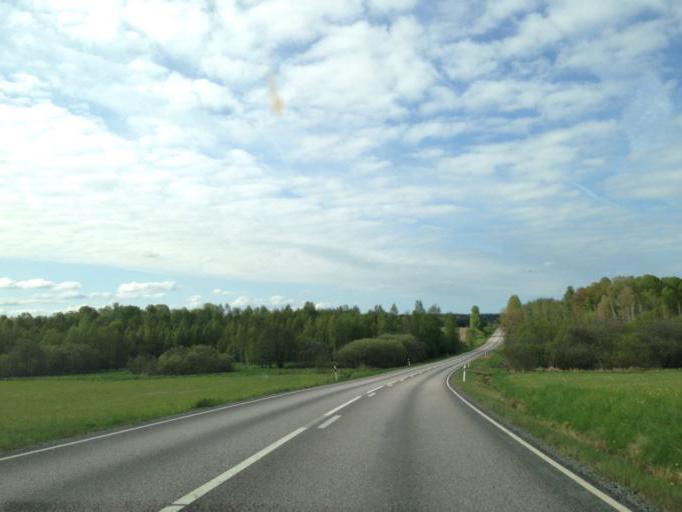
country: SE
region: Soedermanland
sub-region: Flens Kommun
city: Malmkoping
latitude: 58.9865
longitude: 16.8422
